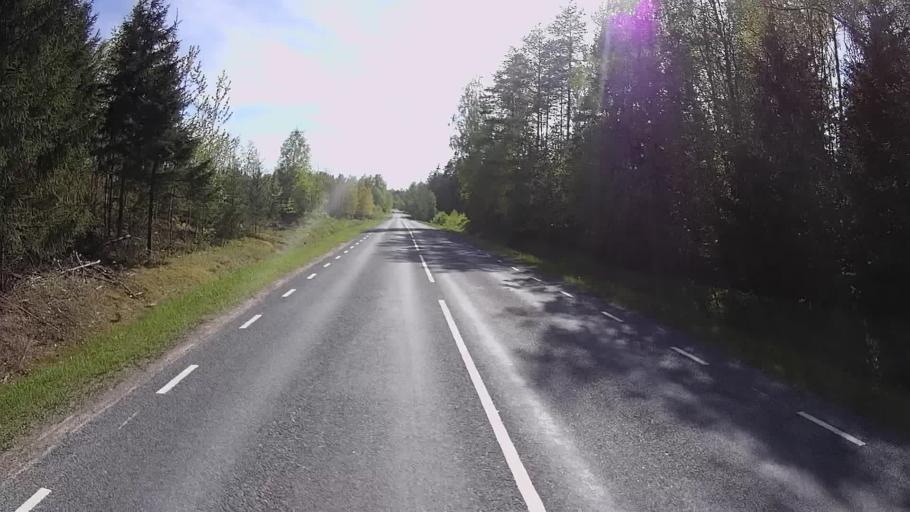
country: EE
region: Vorumaa
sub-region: Antsla vald
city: Vana-Antsla
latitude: 57.9835
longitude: 26.4737
